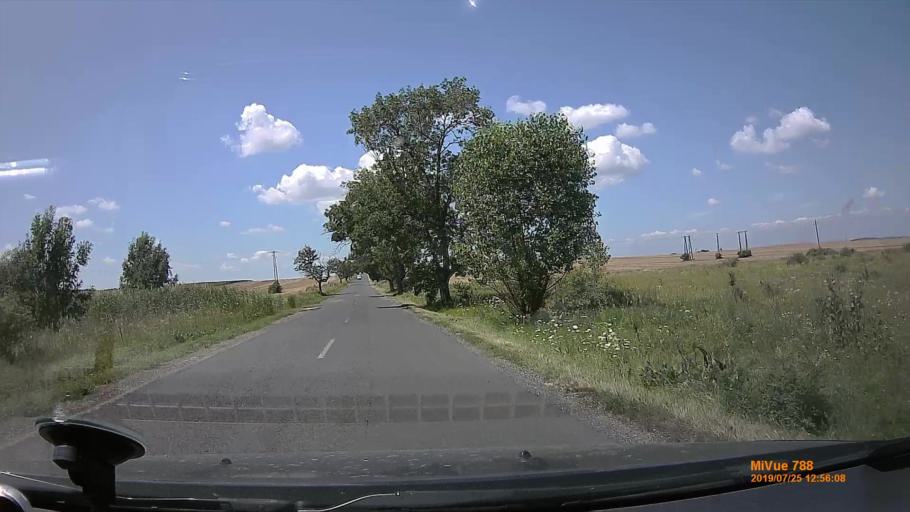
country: HU
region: Borsod-Abauj-Zemplen
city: Abaujszanto
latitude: 48.3129
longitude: 21.1768
